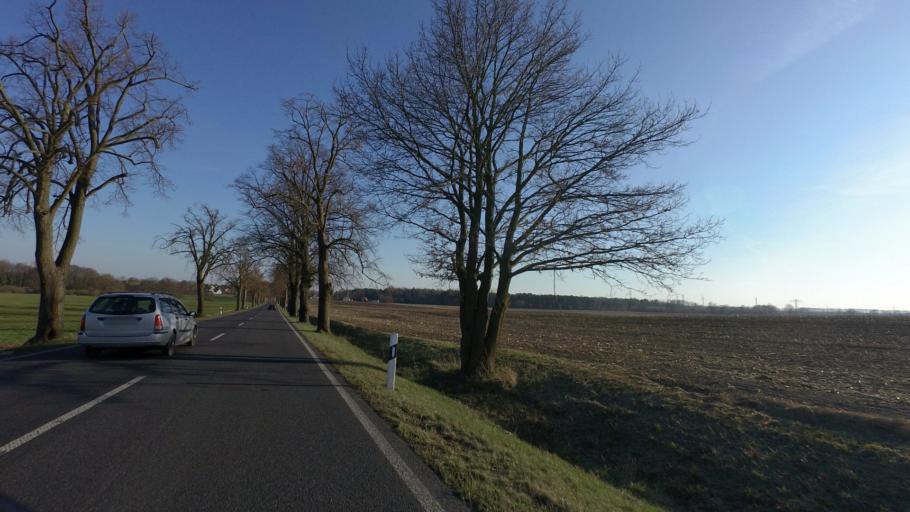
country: DE
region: Brandenburg
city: Britz
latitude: 52.8952
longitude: 13.8039
